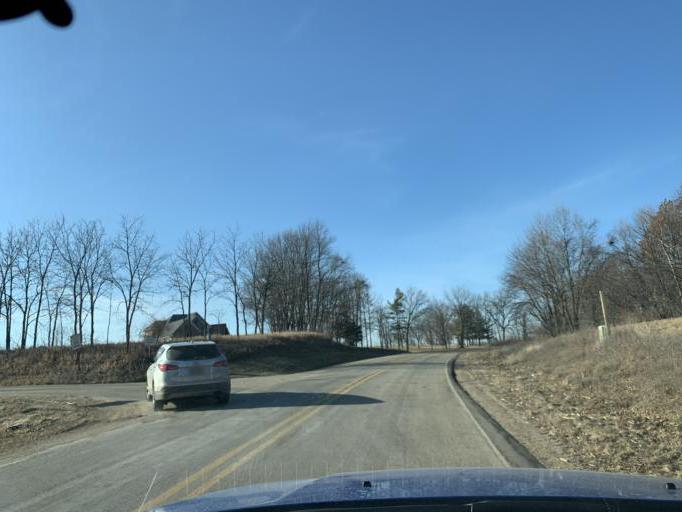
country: US
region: Wisconsin
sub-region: Iowa County
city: Barneveld
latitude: 42.8058
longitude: -89.8795
